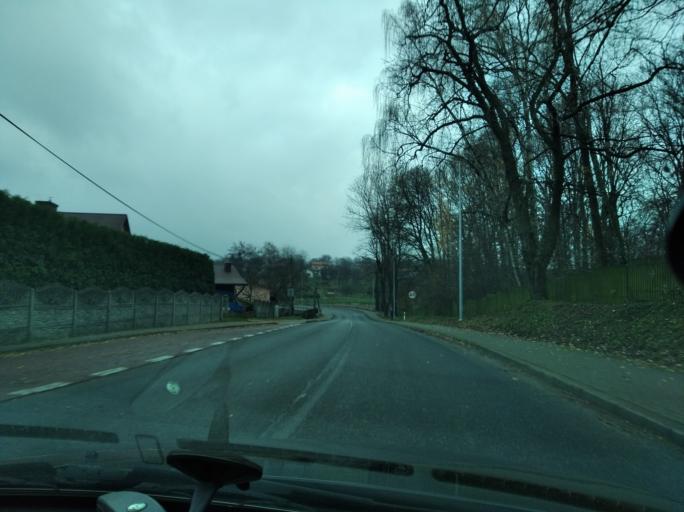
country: PL
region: Subcarpathian Voivodeship
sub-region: Powiat przeworski
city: Sietesz
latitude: 49.9994
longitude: 22.3524
